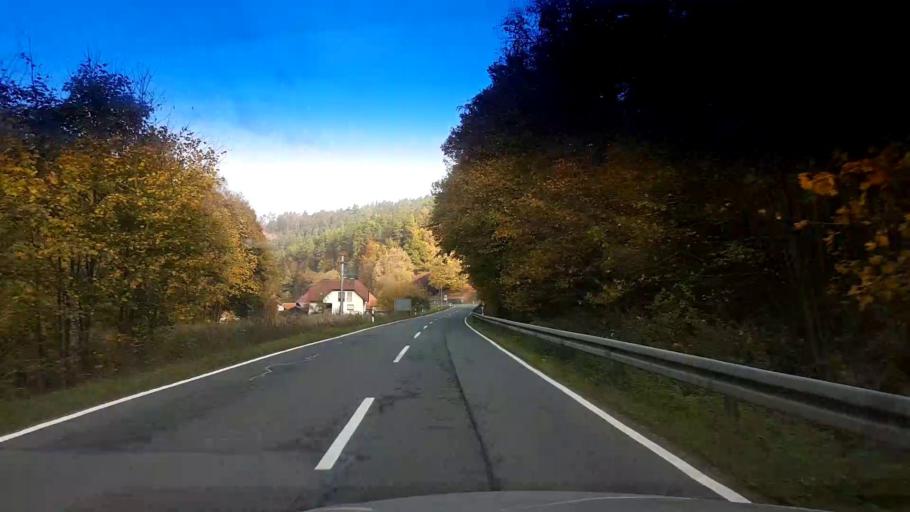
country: DE
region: Bavaria
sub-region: Upper Franconia
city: Weismain
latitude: 50.0492
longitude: 11.2300
